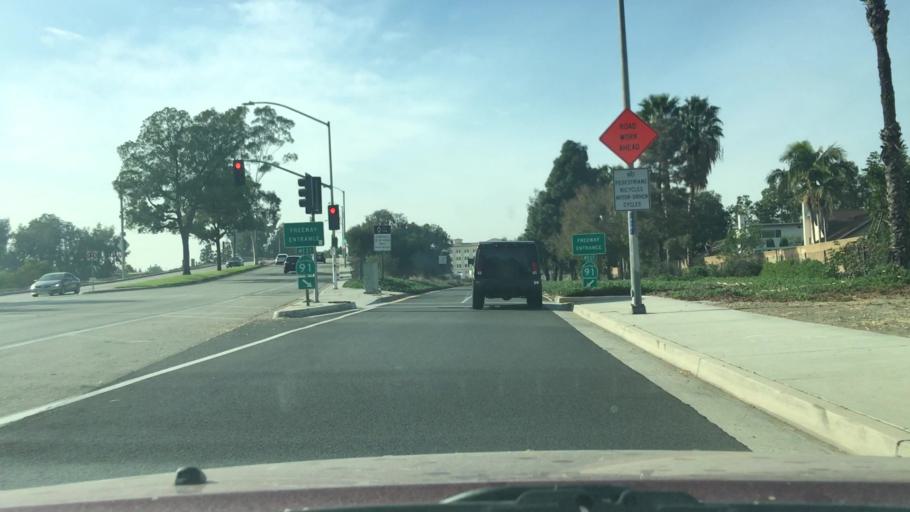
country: US
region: California
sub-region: Los Angeles County
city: Cerritos
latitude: 33.8733
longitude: -118.0578
